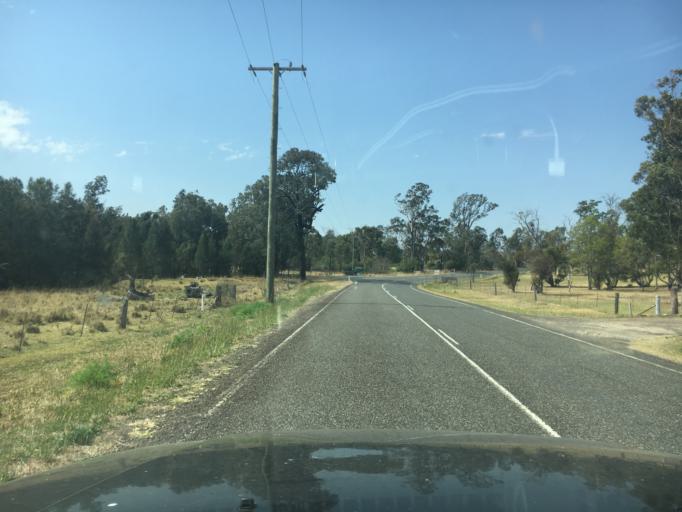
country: AU
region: New South Wales
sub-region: Singleton
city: Singleton
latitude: -32.5446
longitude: 151.2438
